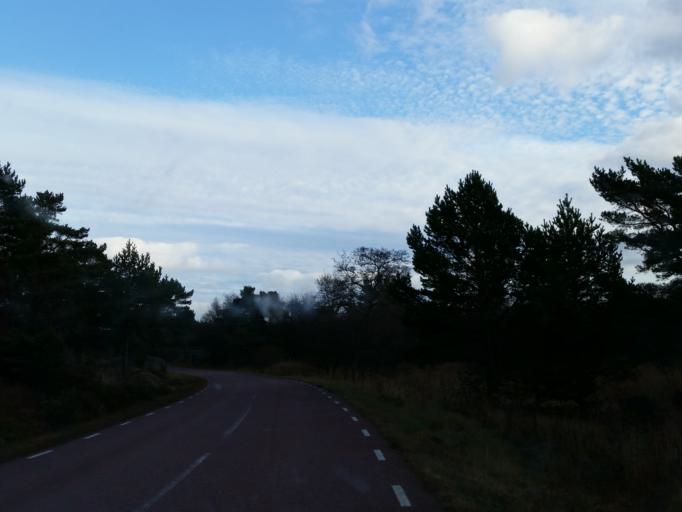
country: AX
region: Alands skaergard
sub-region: Foegloe
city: Foegloe
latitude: 60.0544
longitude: 20.5114
